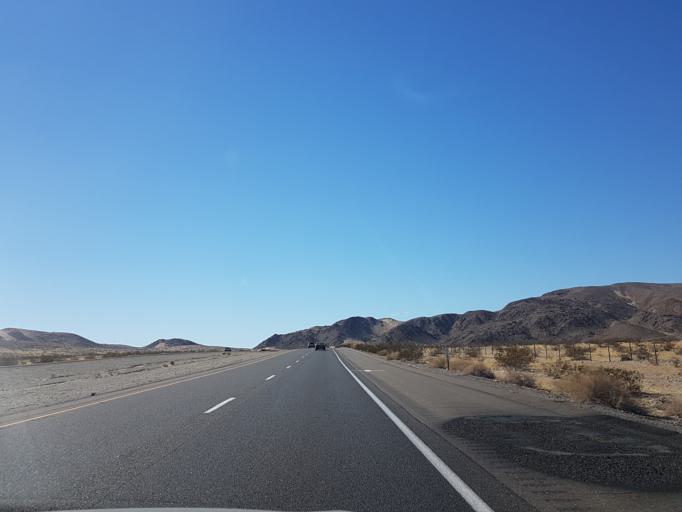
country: US
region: California
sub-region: San Bernardino County
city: Fort Irwin
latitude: 35.0852
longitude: -116.3660
